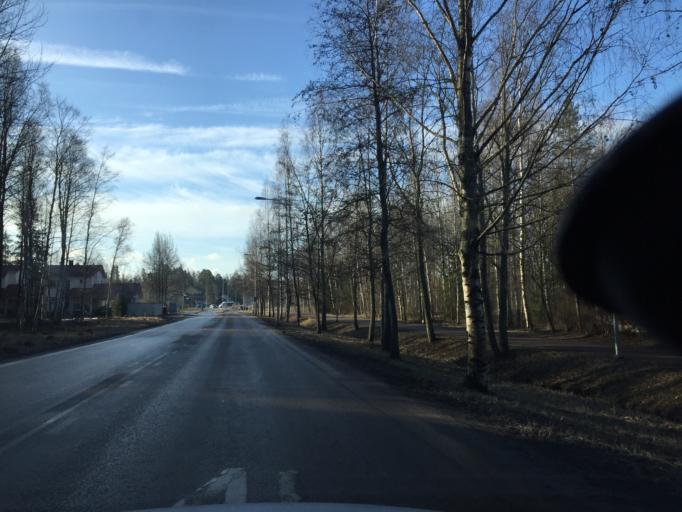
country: FI
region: Uusimaa
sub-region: Helsinki
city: Teekkarikylae
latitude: 60.2803
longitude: 24.8725
